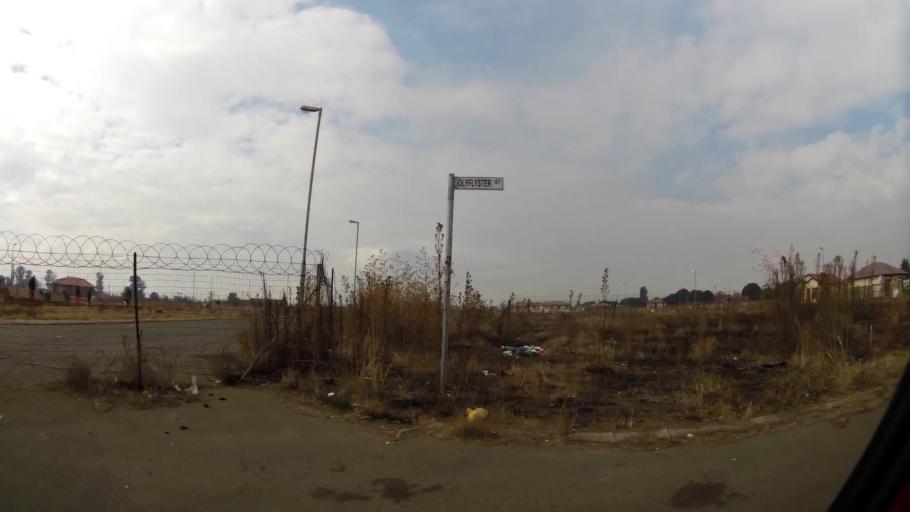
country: ZA
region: Gauteng
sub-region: Sedibeng District Municipality
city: Vanderbijlpark
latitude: -26.6850
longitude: 27.8517
